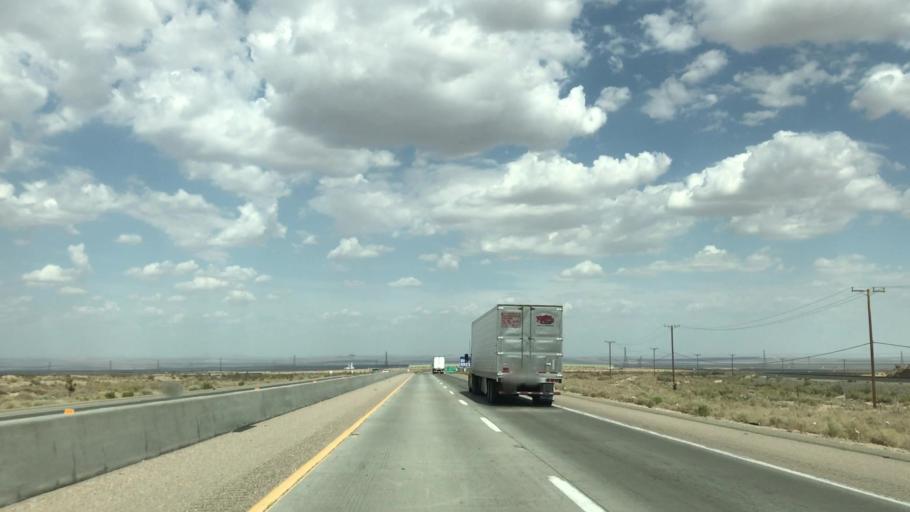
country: US
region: California
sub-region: Kern County
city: Mojave
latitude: 35.1165
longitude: -118.1974
